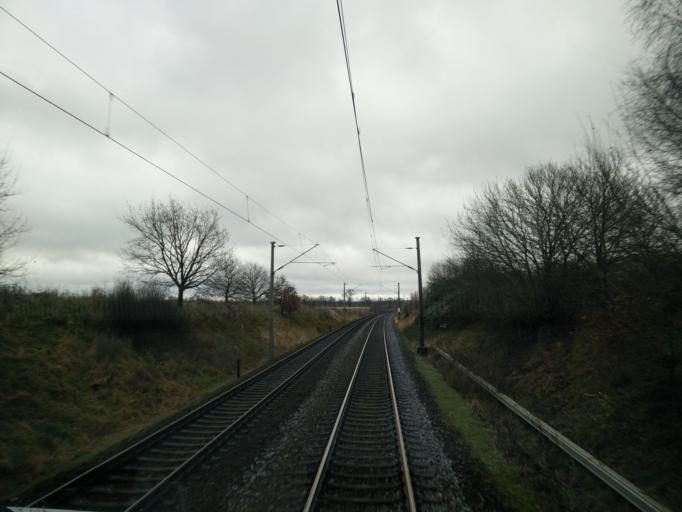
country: DE
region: Mecklenburg-Vorpommern
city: Rastow
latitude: 53.4247
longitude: 11.4565
